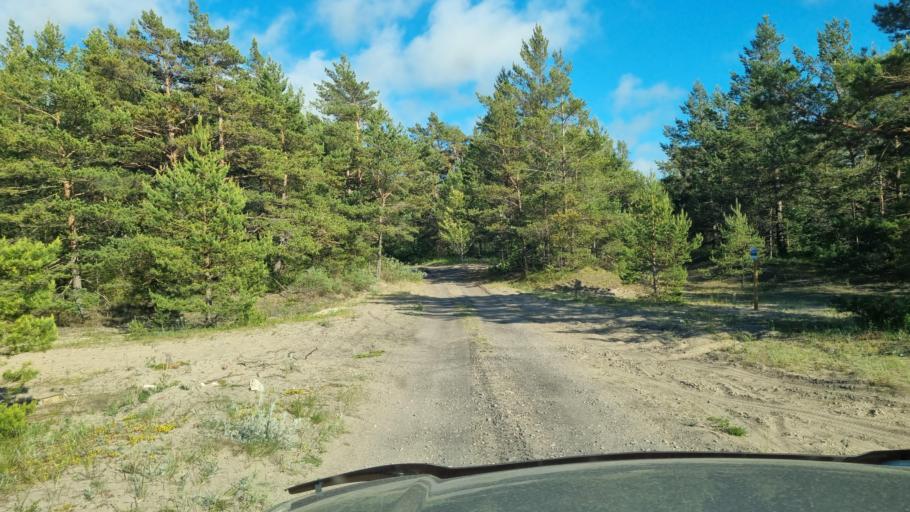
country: LV
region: Ventspils
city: Ventspils
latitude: 57.3642
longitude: 21.5093
